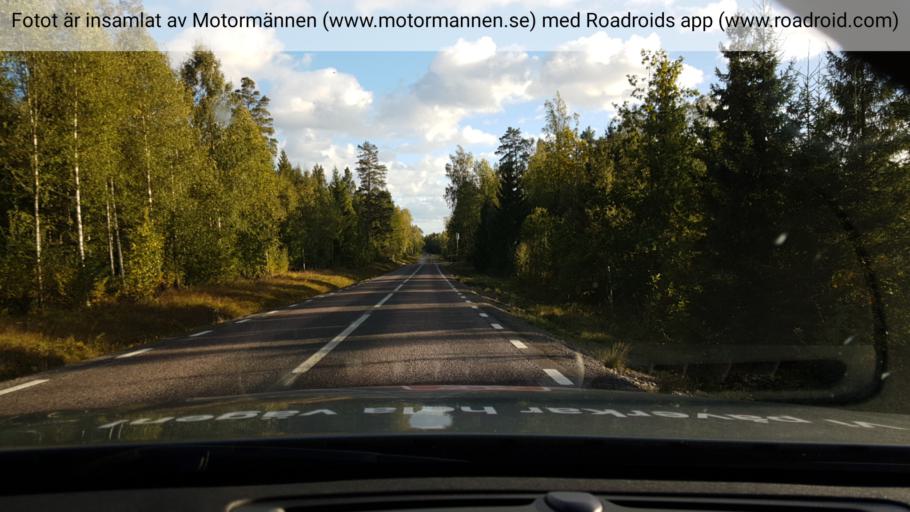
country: SE
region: Vaermland
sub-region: Karlstads Kommun
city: Molkom
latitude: 59.7392
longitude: 13.6784
